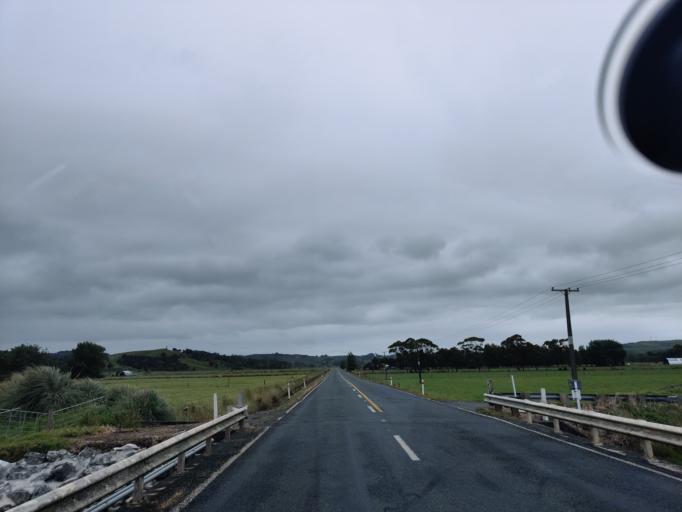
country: NZ
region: Northland
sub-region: Kaipara District
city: Dargaville
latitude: -36.1191
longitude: 174.0750
